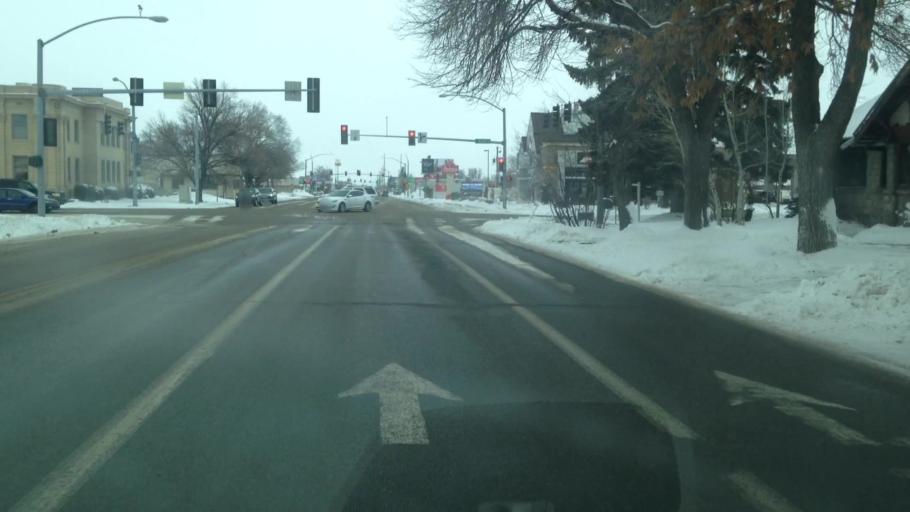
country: US
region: Idaho
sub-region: Madison County
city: Rexburg
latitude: 43.8255
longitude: -111.7781
